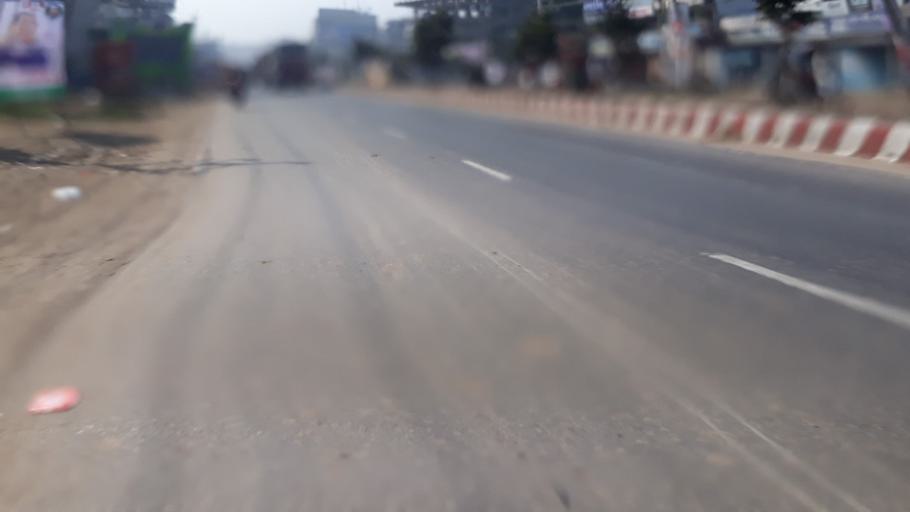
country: BD
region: Dhaka
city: Tungi
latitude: 23.8584
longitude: 90.2623
